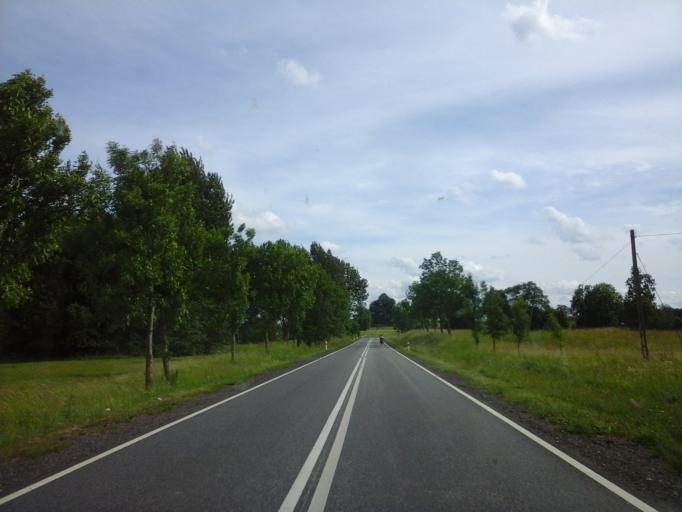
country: PL
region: West Pomeranian Voivodeship
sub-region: Powiat stargardzki
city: Insko
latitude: 53.4708
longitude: 15.5780
